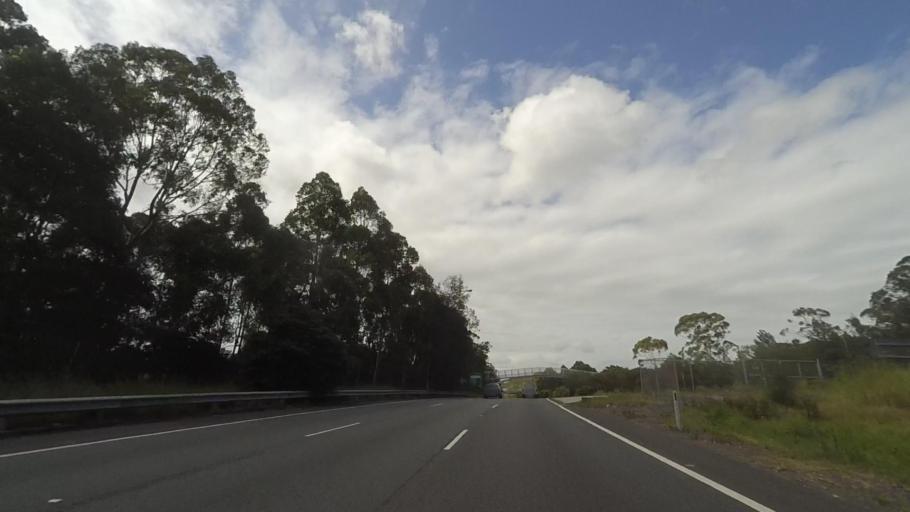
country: AU
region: New South Wales
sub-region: Newcastle
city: North Lambton
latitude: -32.9047
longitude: 151.6927
